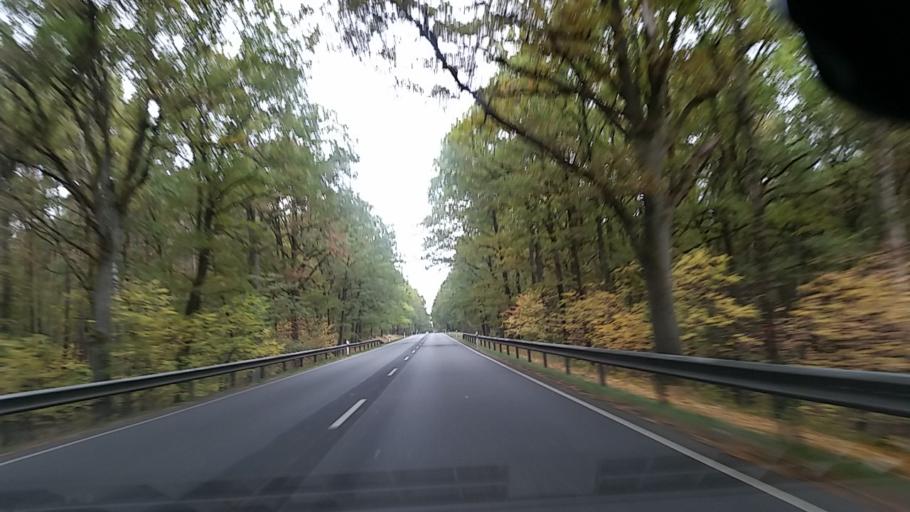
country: DE
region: Lower Saxony
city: Sprakensehl
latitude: 52.7520
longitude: 10.4909
